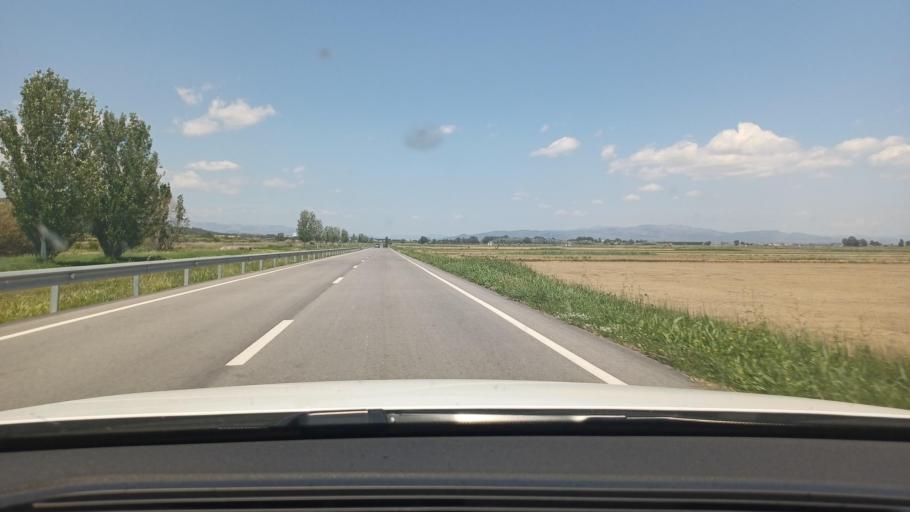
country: ES
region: Catalonia
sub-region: Provincia de Tarragona
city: Sant Carles de la Rapita
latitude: 40.6504
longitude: 0.5968
